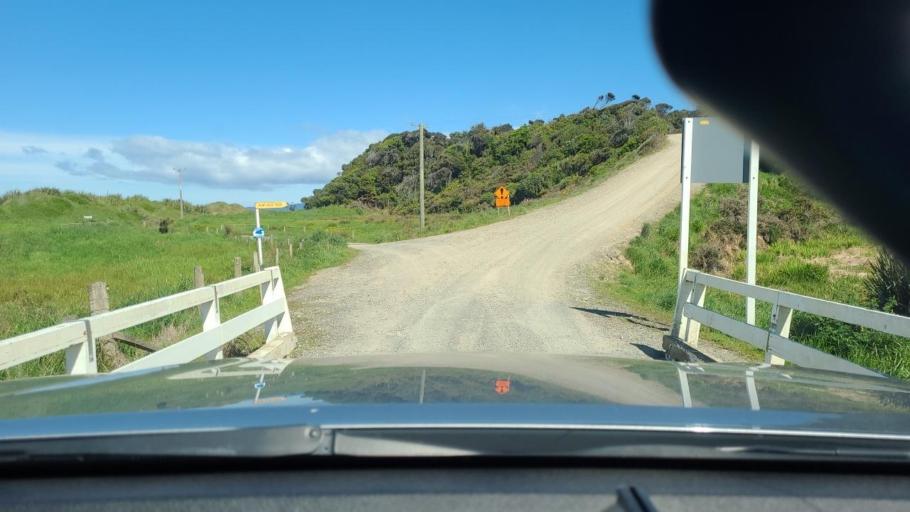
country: NZ
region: Southland
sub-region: Southland District
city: Riverton
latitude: -46.1561
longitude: 167.5178
